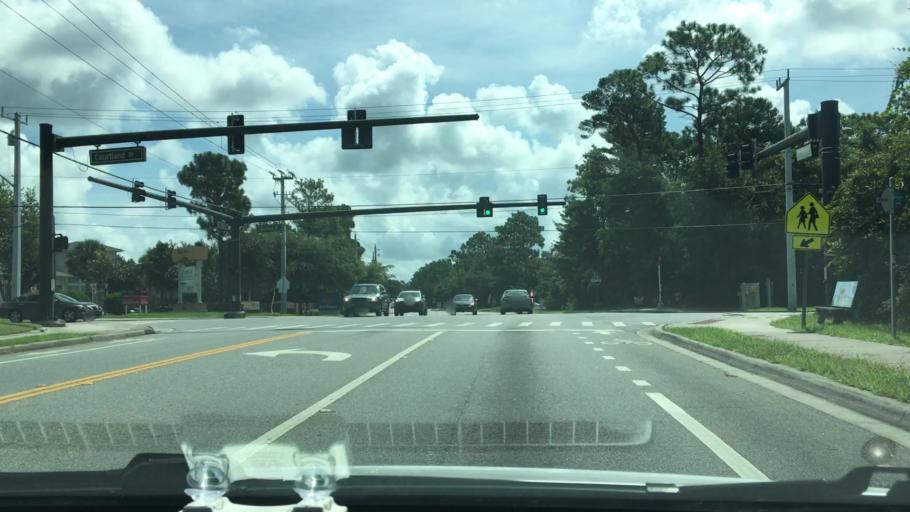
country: US
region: Florida
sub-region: Volusia County
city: Deltona
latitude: 28.8785
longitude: -81.1791
